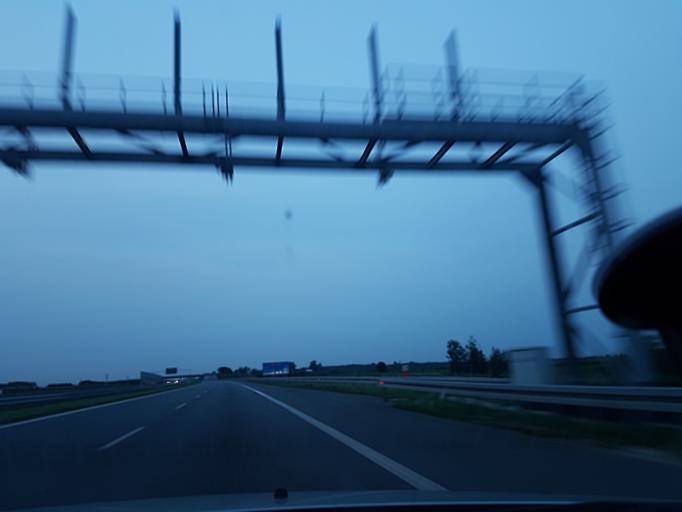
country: PL
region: Lodz Voivodeship
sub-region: Powiat leczycki
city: Piatek
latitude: 52.0534
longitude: 19.5356
